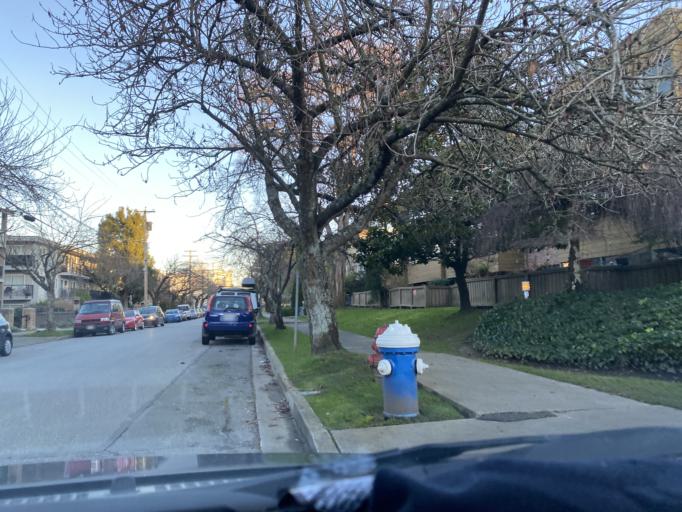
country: CA
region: British Columbia
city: West End
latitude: 49.2646
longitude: -123.1481
